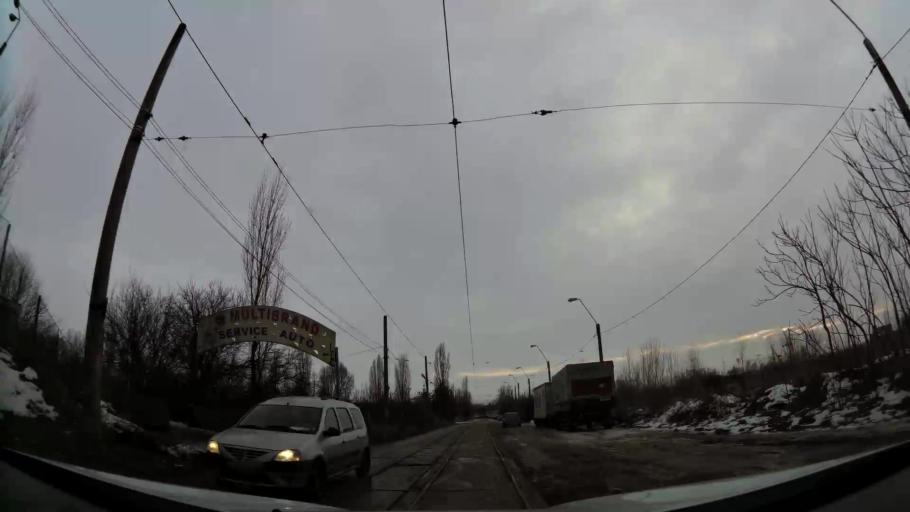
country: RO
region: Ilfov
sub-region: Comuna Glina
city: Catelu
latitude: 44.4030
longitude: 26.2024
